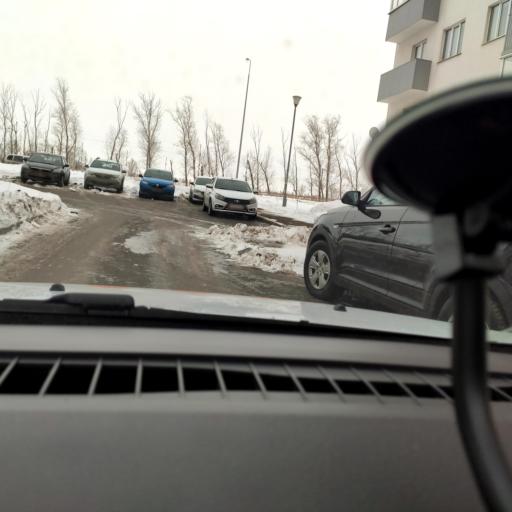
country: RU
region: Samara
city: Samara
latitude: 53.0919
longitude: 50.1608
